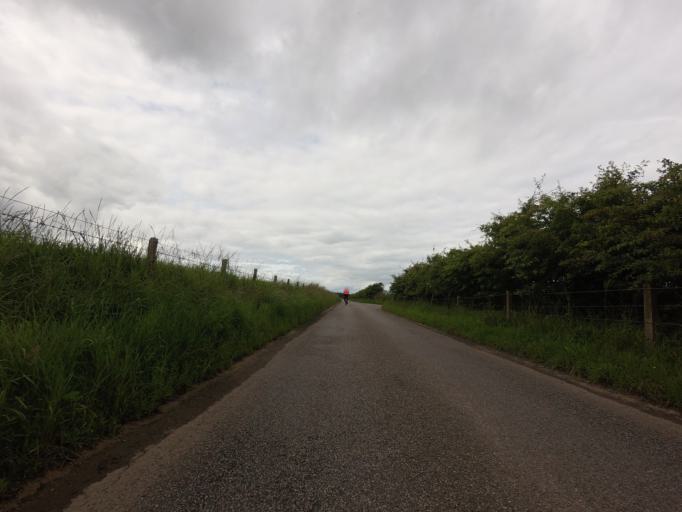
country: GB
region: Scotland
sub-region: Moray
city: Forres
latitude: 57.6223
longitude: -3.6684
